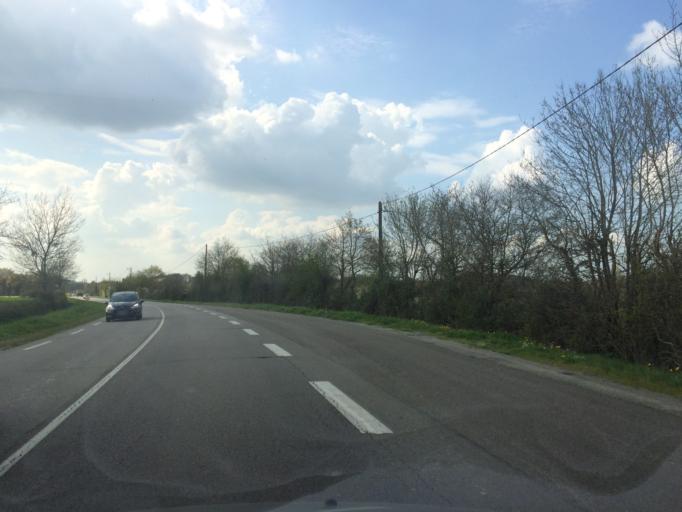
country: FR
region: Pays de la Loire
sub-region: Departement de la Loire-Atlantique
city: Blain
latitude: 47.4664
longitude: -1.7108
